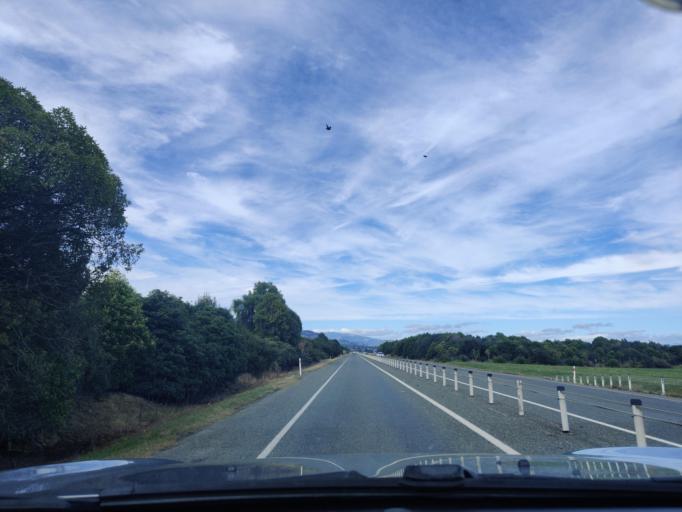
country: NZ
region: Tasman
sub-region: Tasman District
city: Richmond
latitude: -41.3126
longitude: 173.2166
